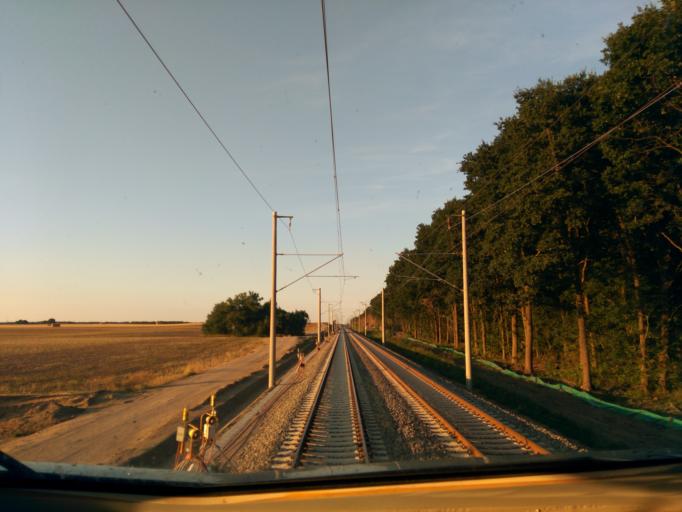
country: DE
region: Mecklenburg-Vorpommern
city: Lubstorf
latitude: 53.7456
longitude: 11.4261
